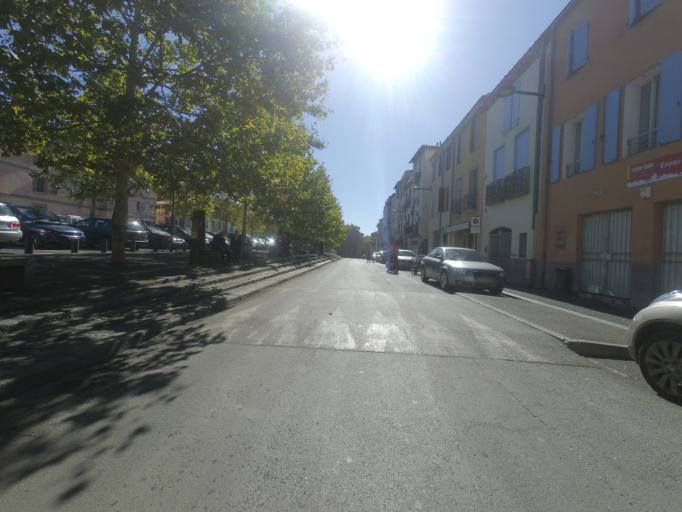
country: FR
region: Languedoc-Roussillon
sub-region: Departement des Pyrenees-Orientales
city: Perpignan
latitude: 42.6986
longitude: 2.9010
